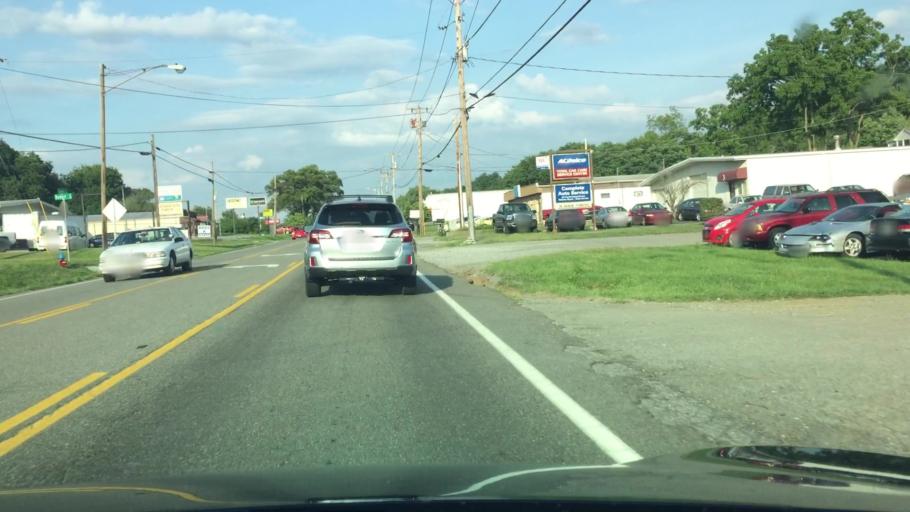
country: US
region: Virginia
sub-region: Montgomery County
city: Christiansburg
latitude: 37.1274
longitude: -80.4263
